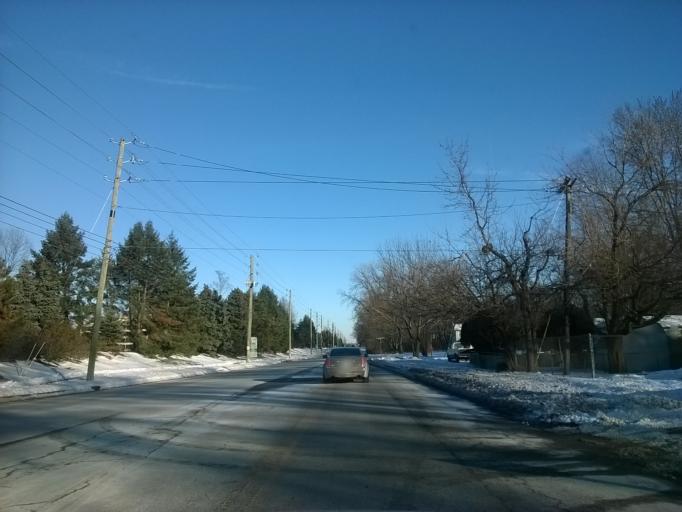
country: US
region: Indiana
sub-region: Marion County
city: Meridian Hills
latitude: 39.9270
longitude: -86.1549
